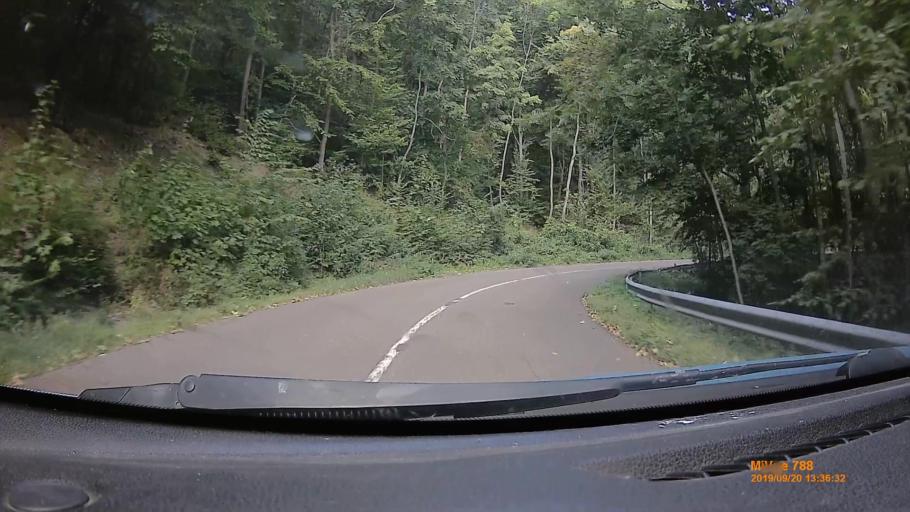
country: HU
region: Heves
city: Szilvasvarad
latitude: 48.0563
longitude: 20.5151
